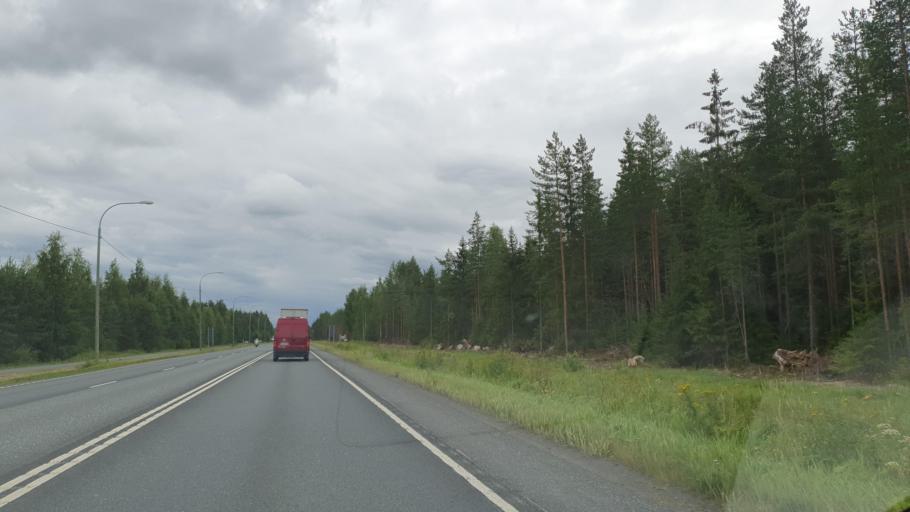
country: FI
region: Northern Savo
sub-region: Ylae-Savo
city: Iisalmi
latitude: 63.4794
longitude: 27.2953
